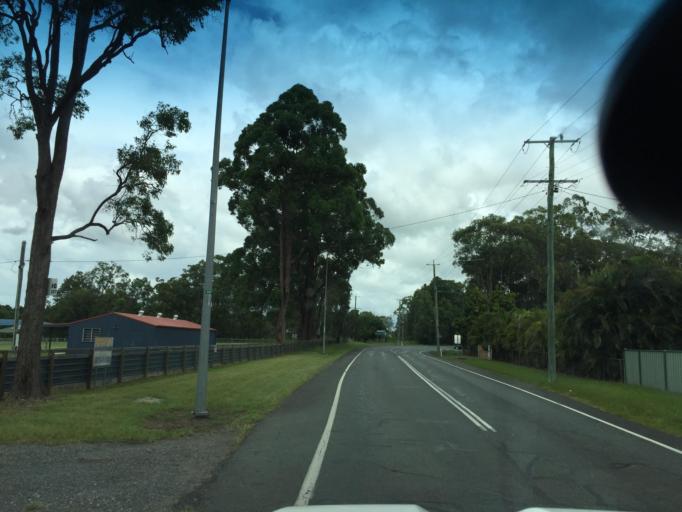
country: AU
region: Queensland
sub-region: Moreton Bay
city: Caboolture
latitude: -27.0585
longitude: 152.9104
